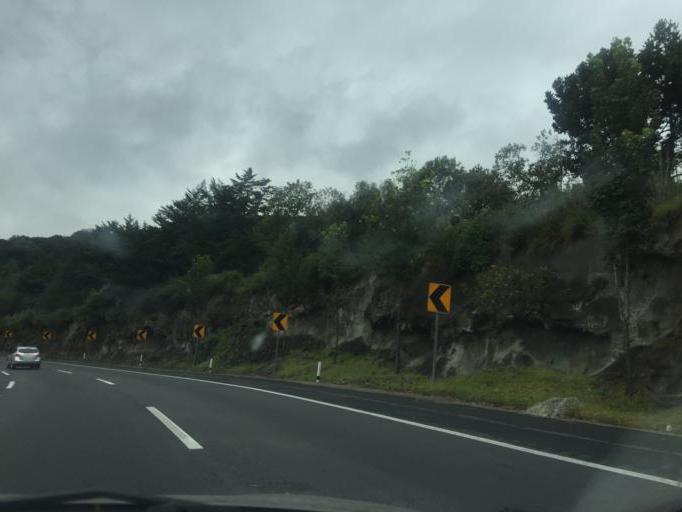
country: MX
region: Mexico City
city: Xochimilco
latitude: 19.2235
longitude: -99.1436
